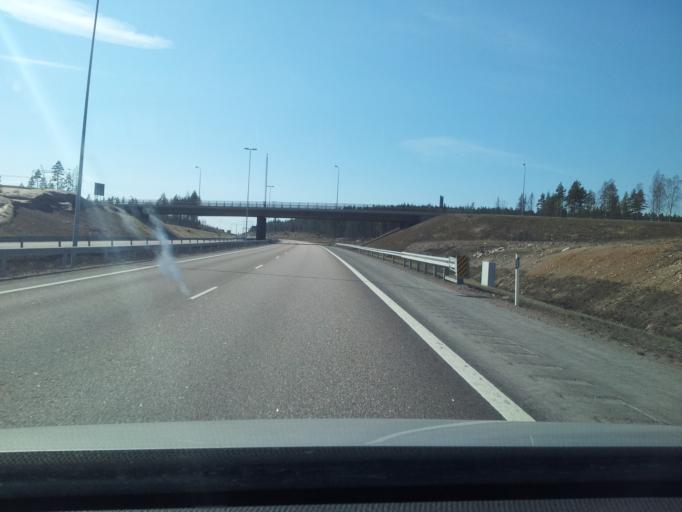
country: FI
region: Uusimaa
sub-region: Loviisa
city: Ruotsinpyhtaeae
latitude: 60.4925
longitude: 26.4213
